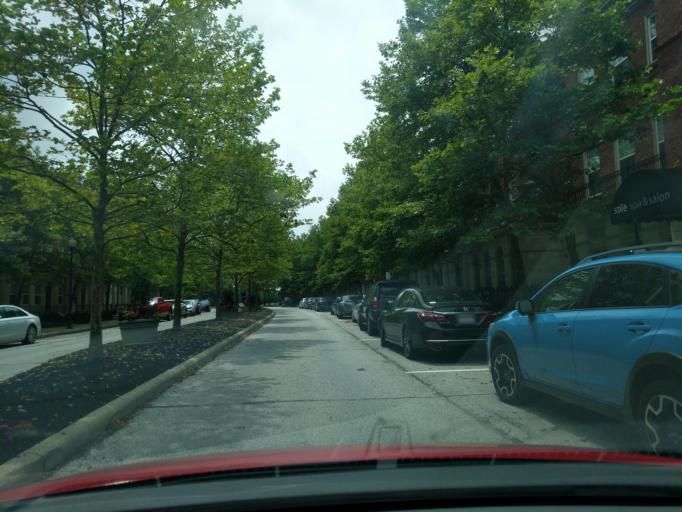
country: US
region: Ohio
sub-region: Franklin County
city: Minerva Park
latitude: 40.0476
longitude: -82.9155
